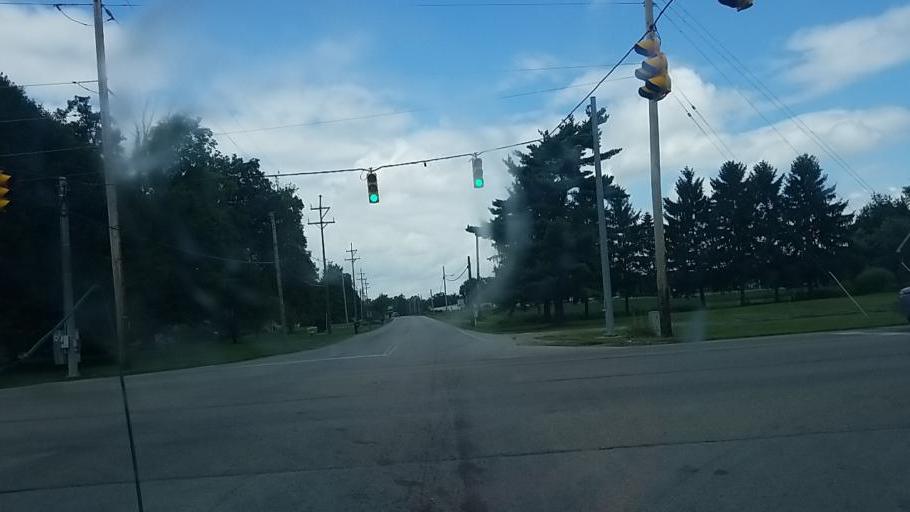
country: US
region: Ohio
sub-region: Clark County
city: Springfield
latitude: 39.8934
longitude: -83.7900
